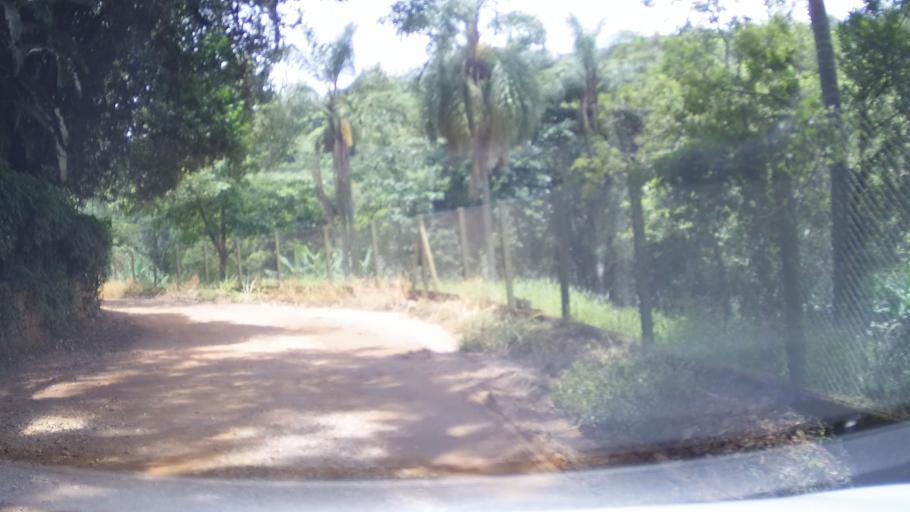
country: BR
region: Sao Paulo
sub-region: Vinhedo
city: Vinhedo
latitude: -22.9943
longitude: -46.9664
